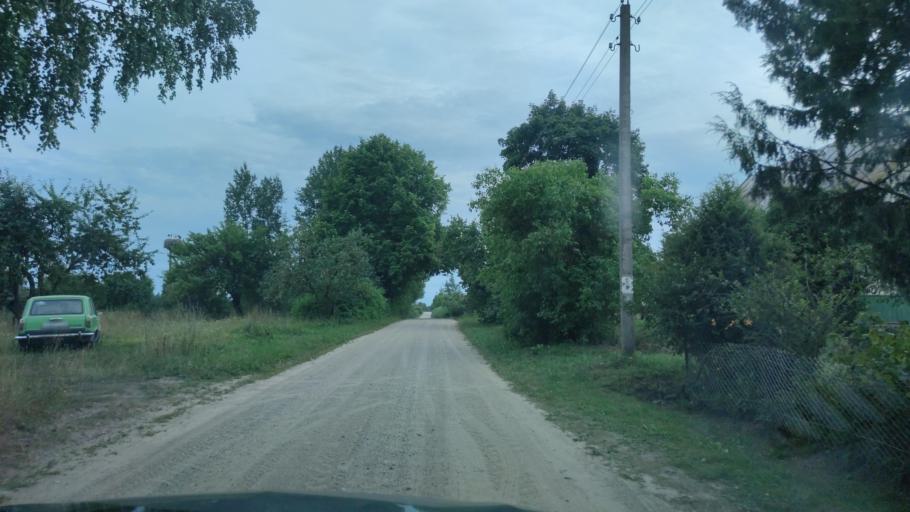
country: BY
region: Vitebsk
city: Mosar
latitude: 55.1279
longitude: 27.1594
